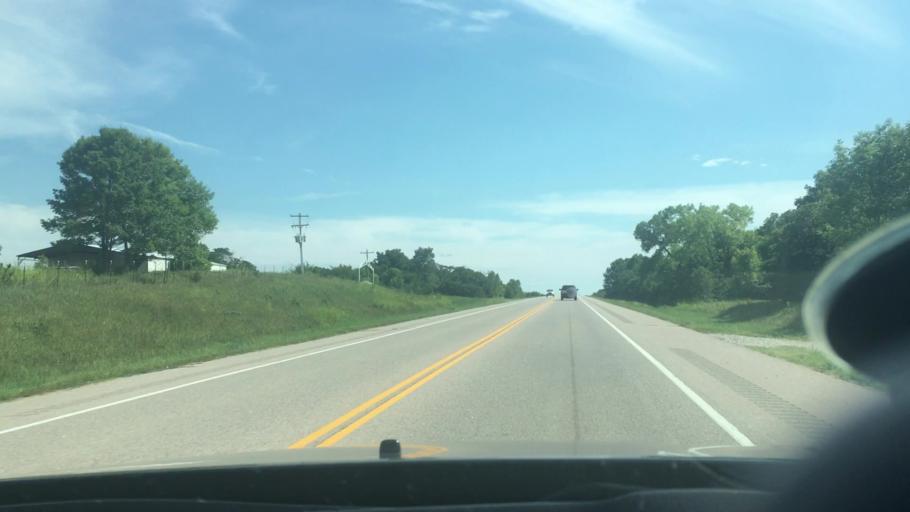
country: US
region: Oklahoma
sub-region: Seminole County
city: Konawa
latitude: 35.0180
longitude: -96.6784
